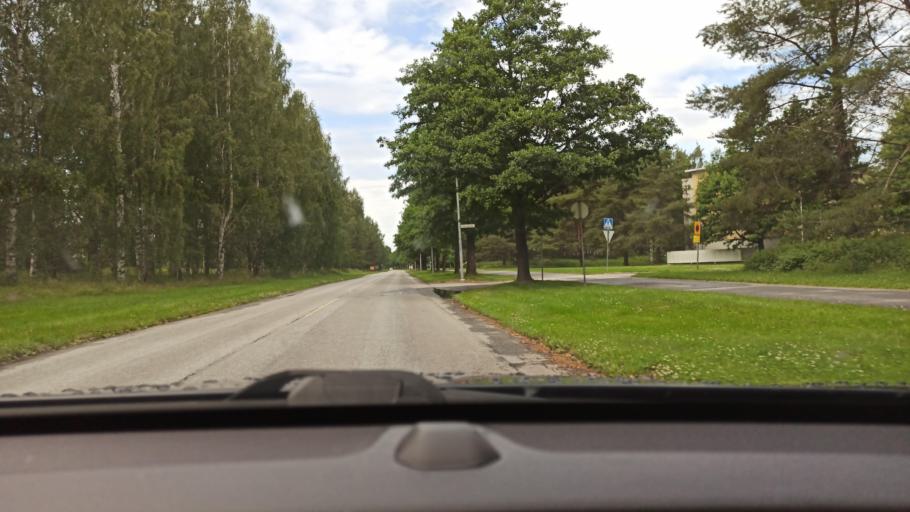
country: FI
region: Satakunta
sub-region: Pori
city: Pori
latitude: 61.4998
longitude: 21.7848
